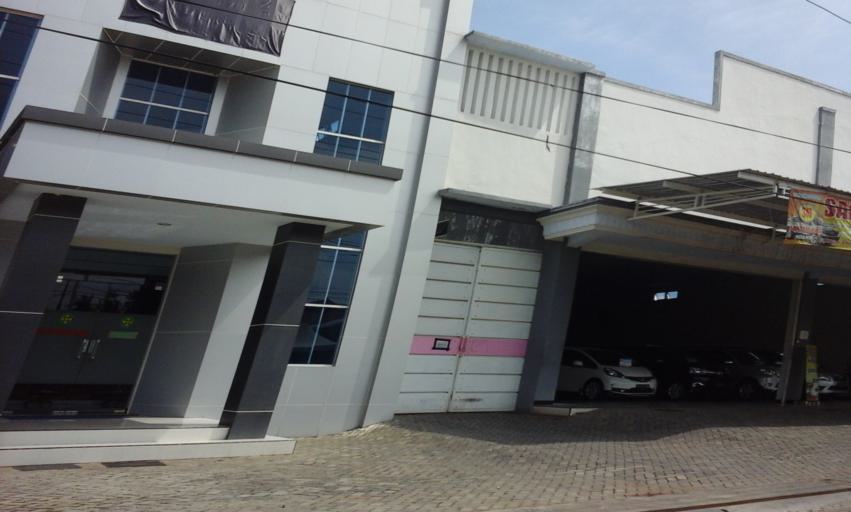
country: ID
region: East Java
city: Krajan
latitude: -8.2462
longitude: 114.3499
